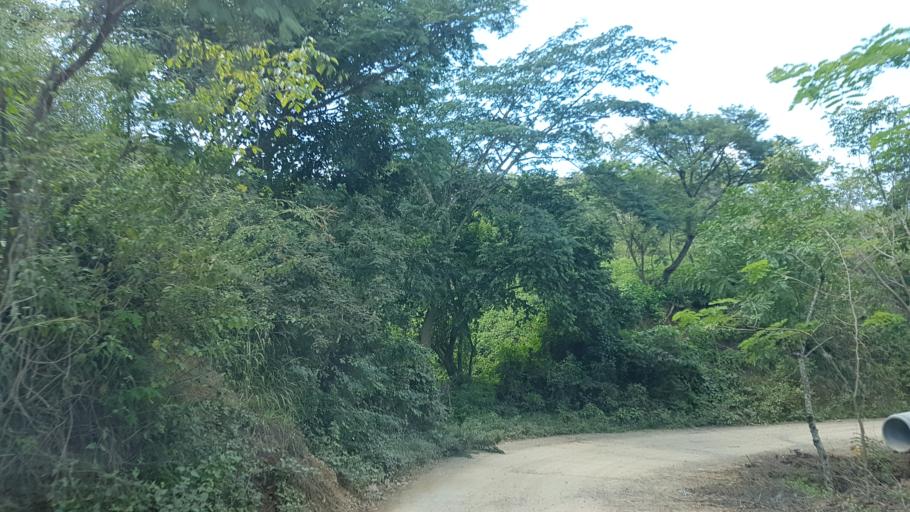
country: HN
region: El Paraiso
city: Oropoli
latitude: 13.7417
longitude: -86.7055
